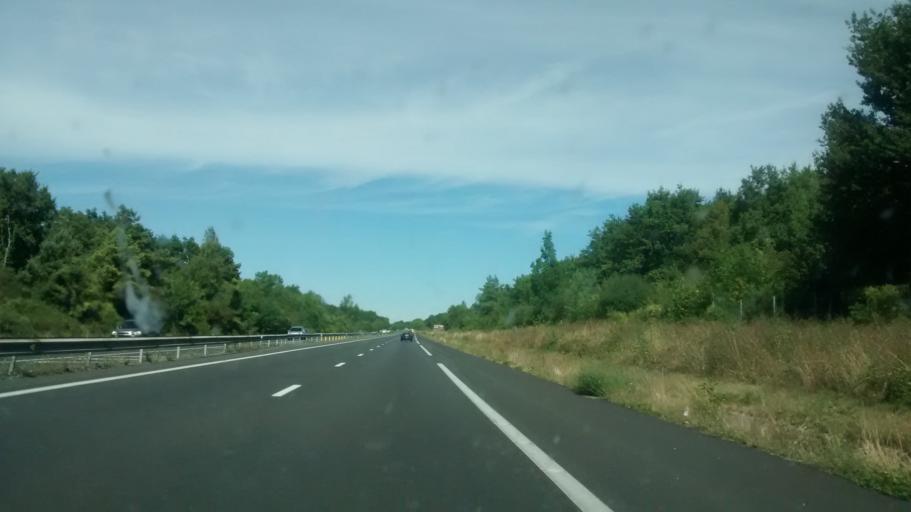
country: FR
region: Poitou-Charentes
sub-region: Departement de la Charente-Maritime
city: Thenac
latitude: 45.6573
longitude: -0.6349
